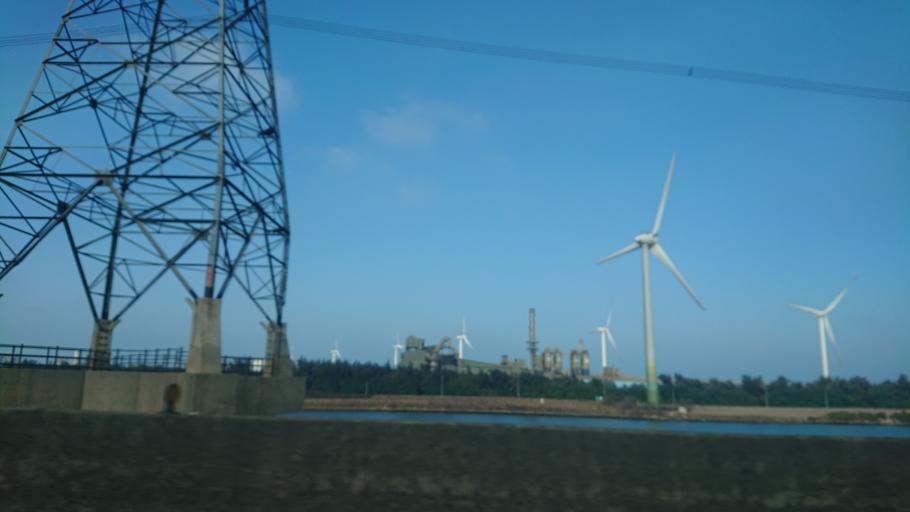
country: TW
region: Taiwan
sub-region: Changhua
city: Chang-hua
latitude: 24.1535
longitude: 120.4558
